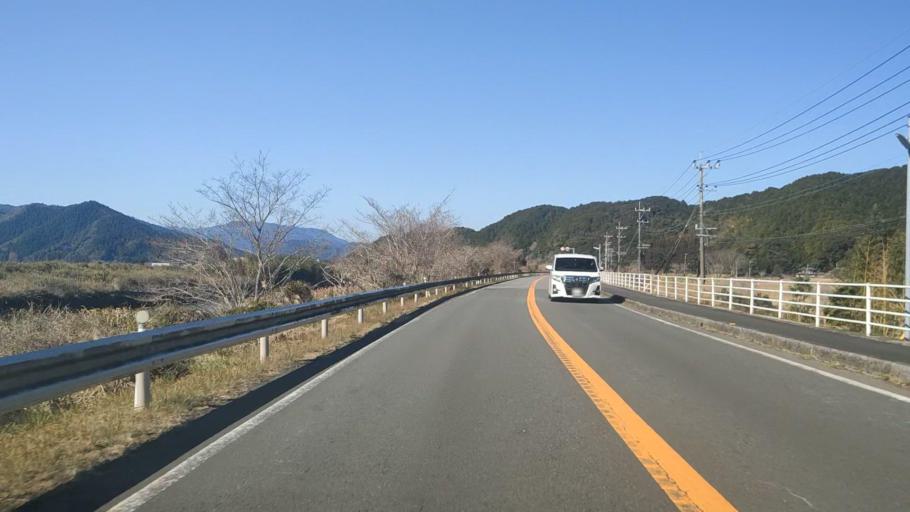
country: JP
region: Oita
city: Saiki
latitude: 32.9369
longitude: 131.9173
